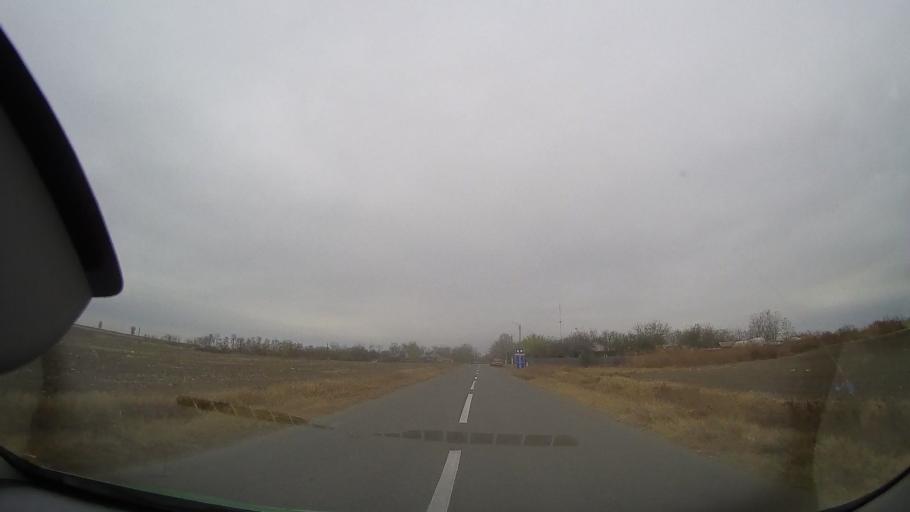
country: RO
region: Braila
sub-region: Comuna Budesti
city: Tataru
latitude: 44.8414
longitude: 27.4260
